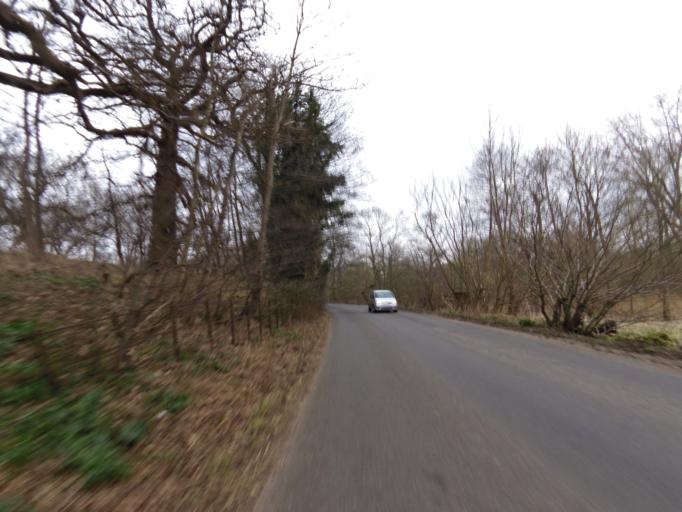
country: GB
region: England
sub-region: Suffolk
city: Wickham Market
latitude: 52.1661
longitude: 1.3563
